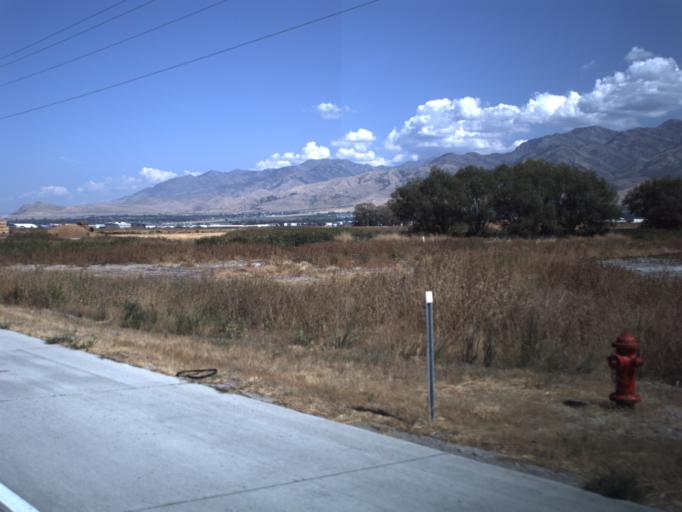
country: US
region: Utah
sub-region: Cache County
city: Logan
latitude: 41.7681
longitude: -111.8585
